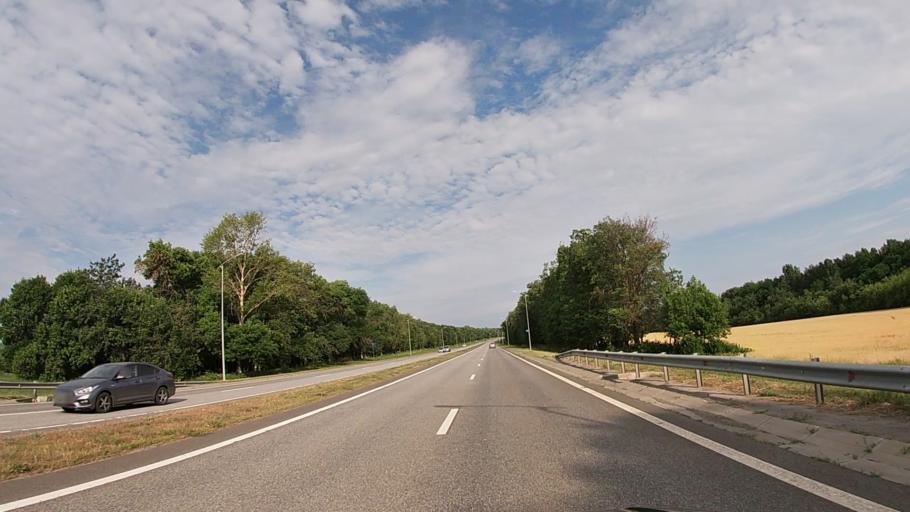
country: RU
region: Belgorod
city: Tomarovka
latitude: 50.6659
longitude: 36.3178
